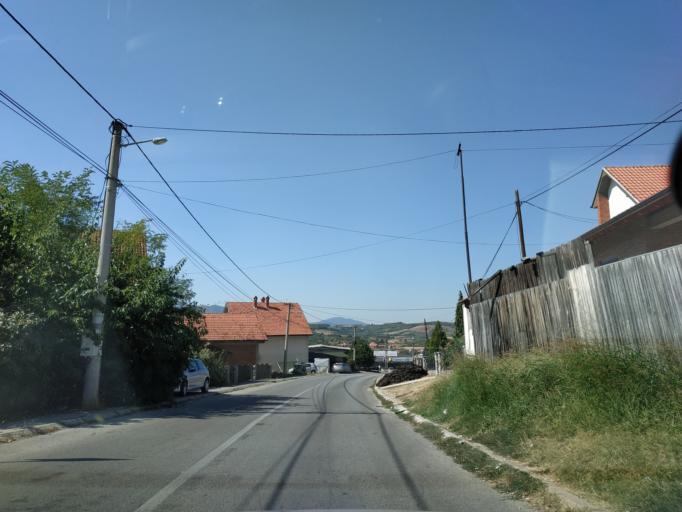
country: RS
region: Central Serbia
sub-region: Sumadijski Okrug
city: Topola
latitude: 44.2557
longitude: 20.6758
